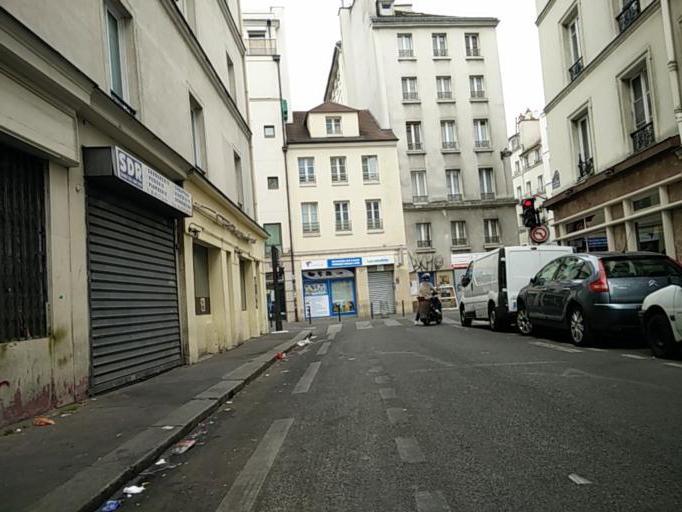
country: FR
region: Ile-de-France
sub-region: Paris
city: Paris
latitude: 48.8676
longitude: 2.3760
